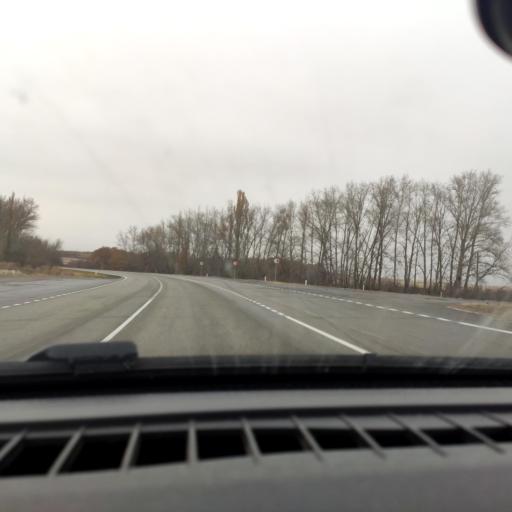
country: RU
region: Voronezj
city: Ostrogozhsk
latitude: 51.0046
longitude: 39.0014
